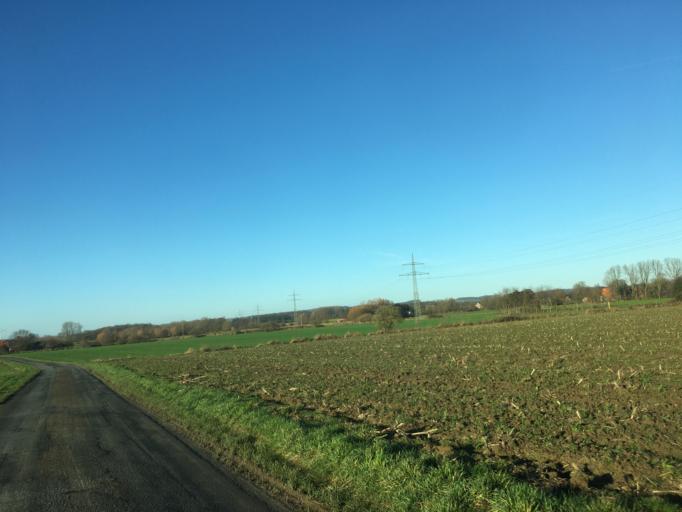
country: DE
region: North Rhine-Westphalia
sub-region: Regierungsbezirk Munster
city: Dulmen
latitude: 51.8691
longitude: 7.2850
